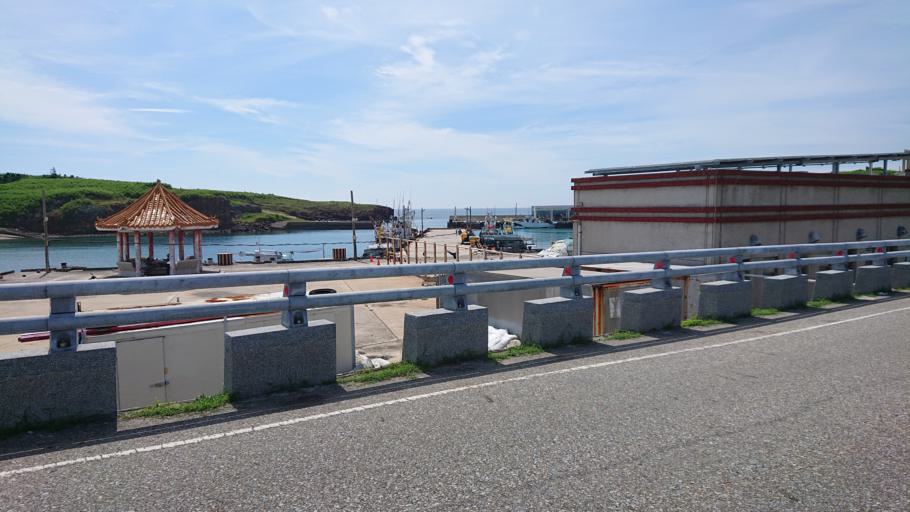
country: TW
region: Taiwan
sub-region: Penghu
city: Ma-kung
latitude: 23.6483
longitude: 119.5198
